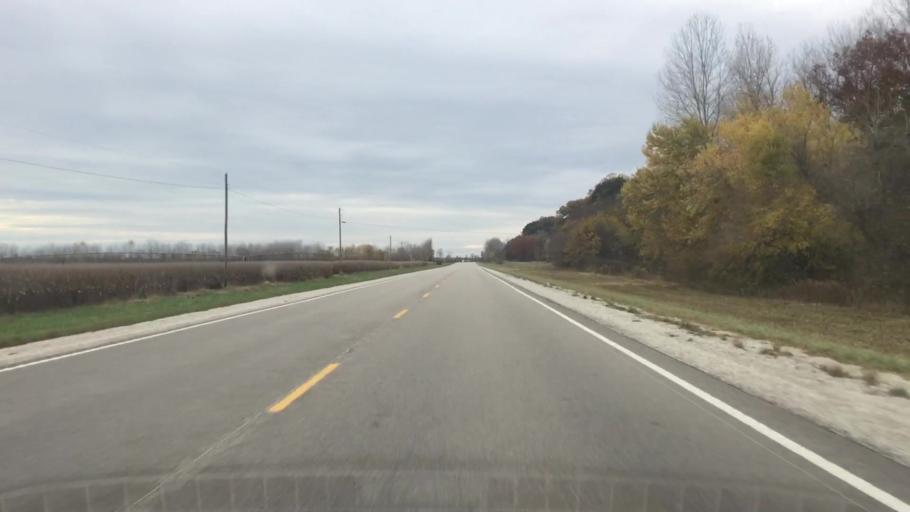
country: US
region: Missouri
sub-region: Callaway County
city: Holts Summit
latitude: 38.5812
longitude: -92.1020
